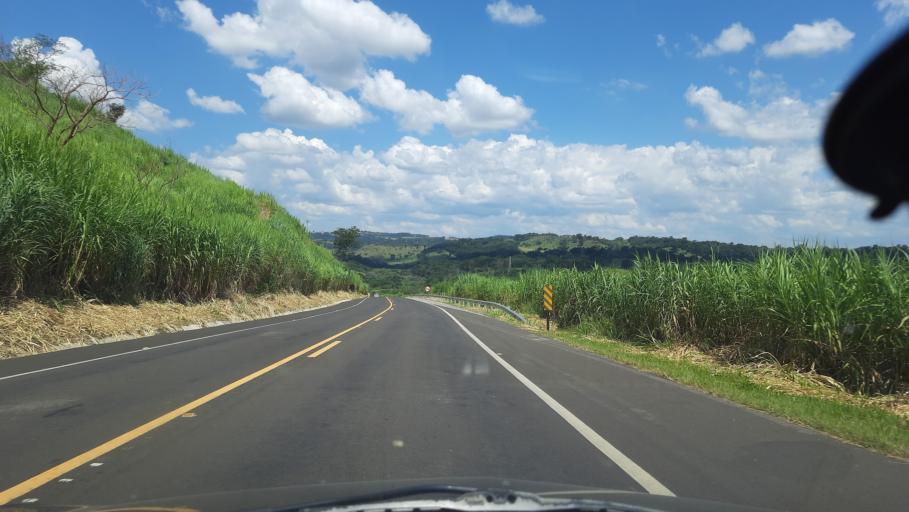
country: BR
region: Sao Paulo
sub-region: Sao Jose Do Rio Pardo
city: Sao Jose do Rio Pardo
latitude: -21.6021
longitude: -46.9788
